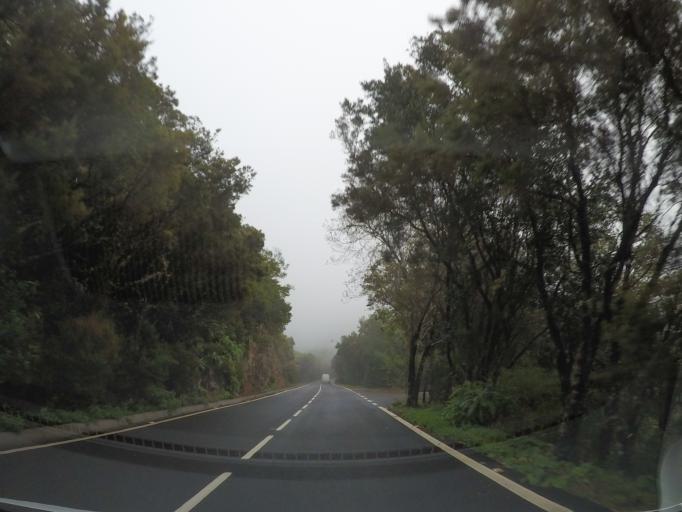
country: ES
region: Canary Islands
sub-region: Provincia de Santa Cruz de Tenerife
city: Vallehermosa
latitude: 28.1245
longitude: -17.2529
